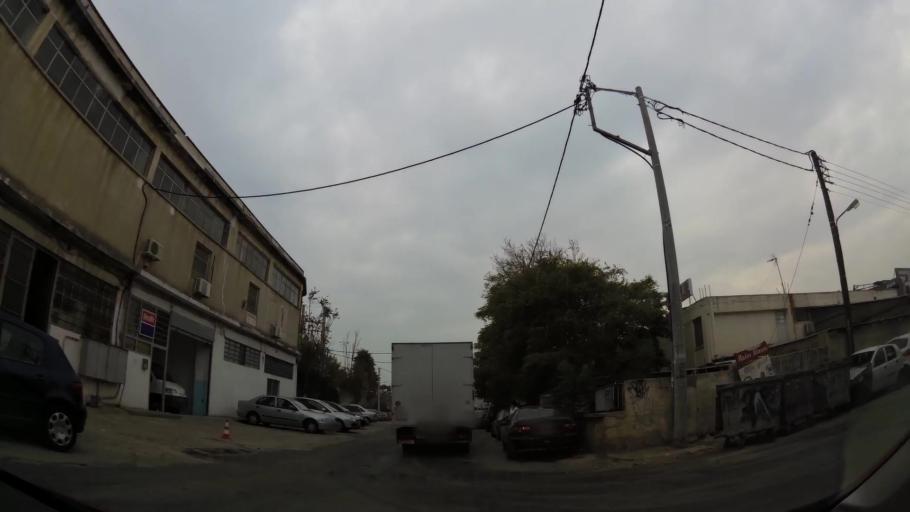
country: GR
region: Attica
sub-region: Nomarchia Athinas
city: Peristeri
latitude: 38.0021
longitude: 23.6977
